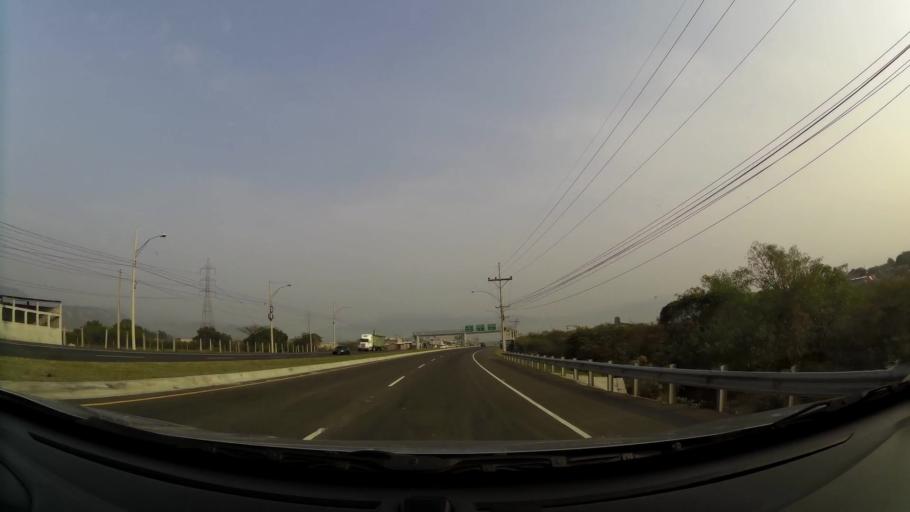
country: HN
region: Francisco Morazan
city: Tamara
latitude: 14.2001
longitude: -87.3448
